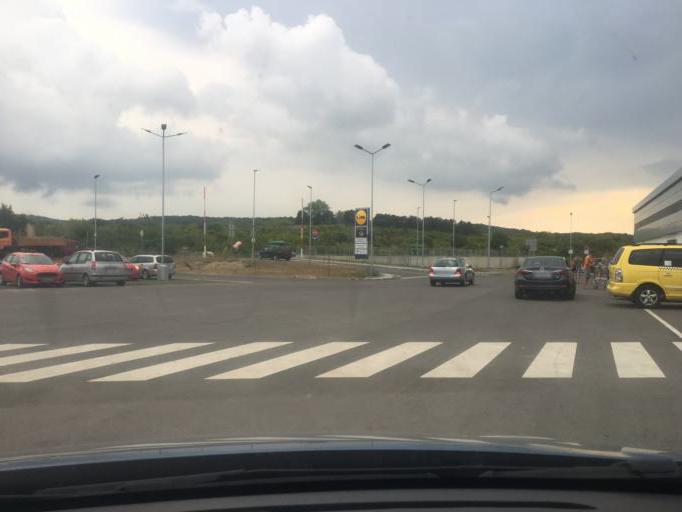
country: BG
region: Burgas
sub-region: Obshtina Sozopol
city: Sozopol
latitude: 42.4062
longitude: 27.7067
